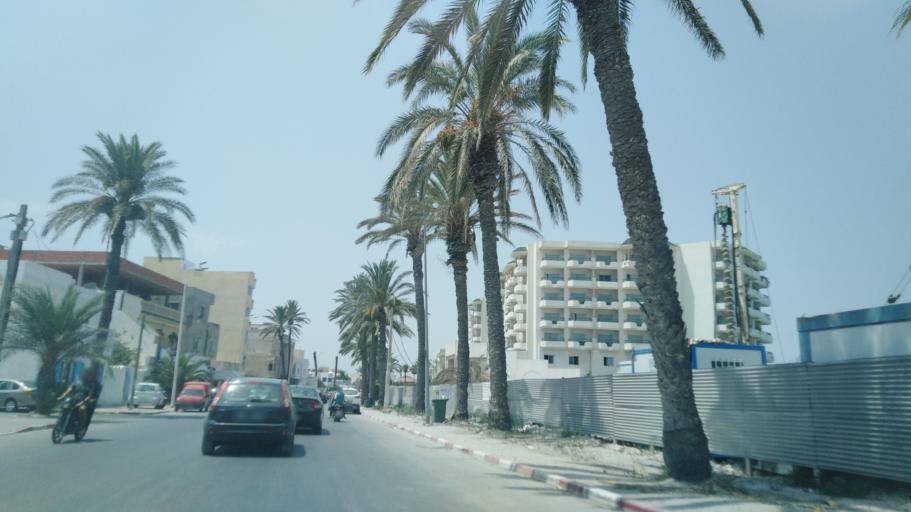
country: TN
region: Al Mahdiyah
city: Mahdia
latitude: 35.5117
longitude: 11.0514
